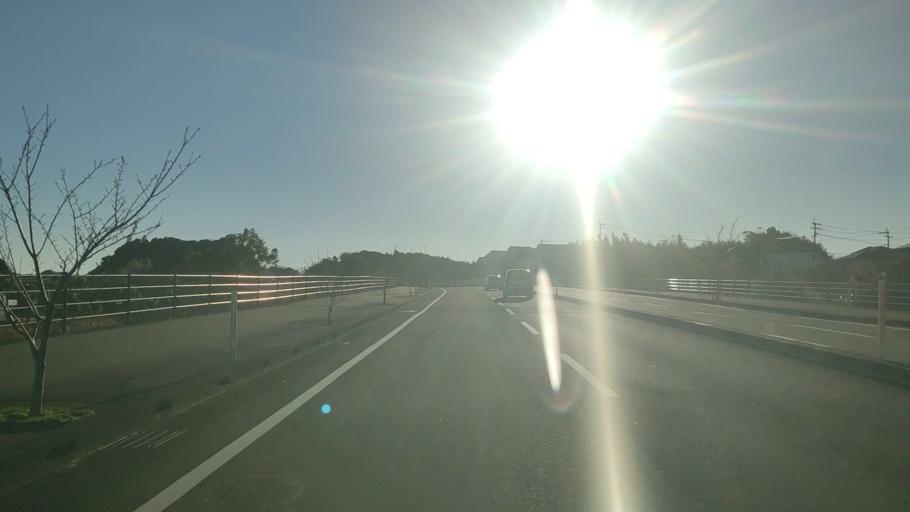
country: JP
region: Miyazaki
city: Miyazaki-shi
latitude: 31.8910
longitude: 131.4044
